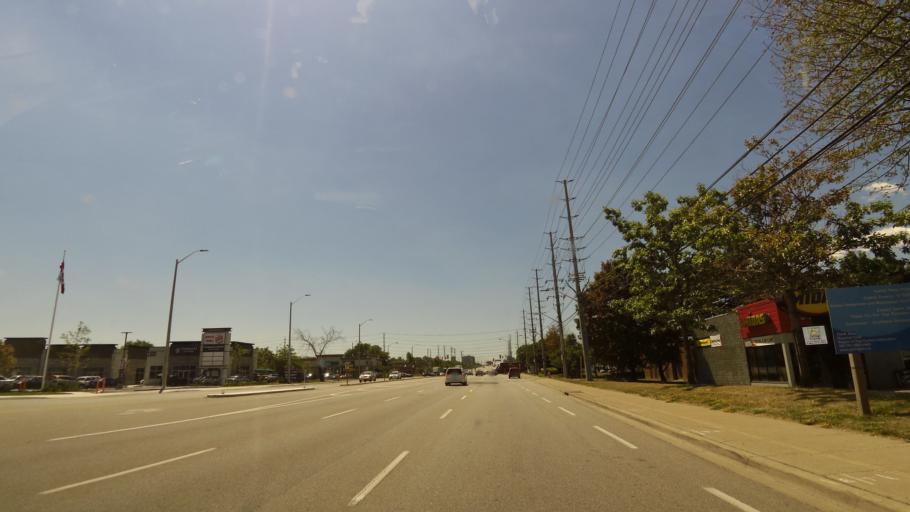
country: CA
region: Ontario
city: Mississauga
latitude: 43.6284
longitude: -79.6291
